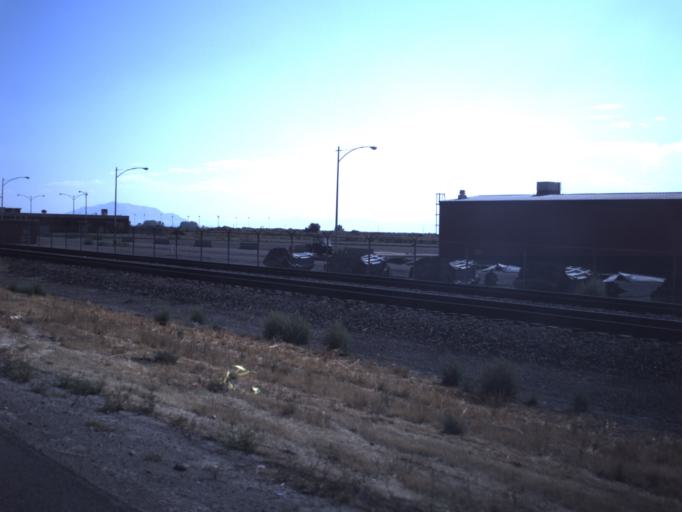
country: US
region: Utah
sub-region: Utah County
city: Lindon
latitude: 40.3205
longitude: -111.7363
